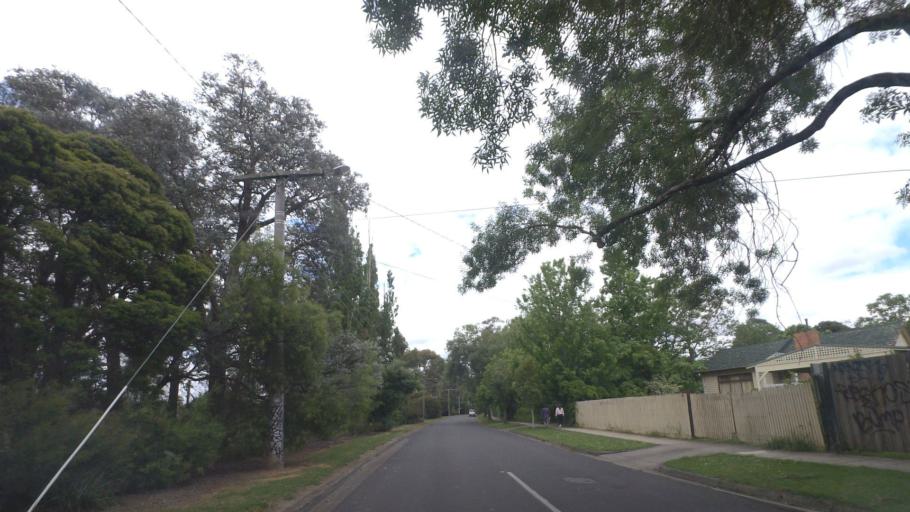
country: AU
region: Victoria
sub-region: Maroondah
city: Croydon North
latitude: -37.7902
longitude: 145.2880
